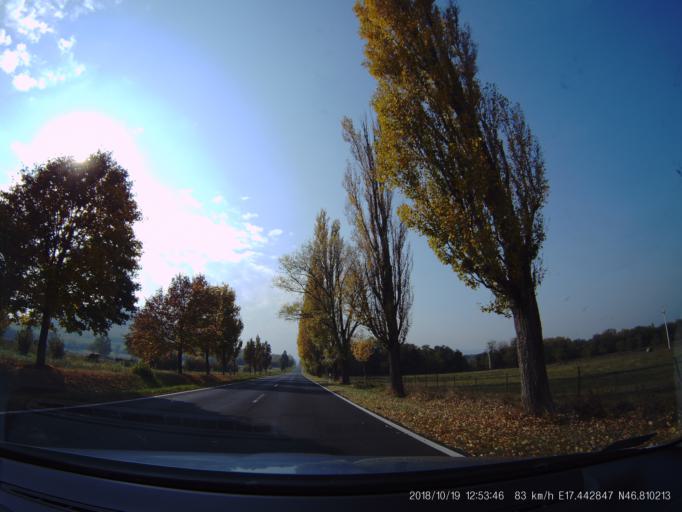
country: HU
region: Veszprem
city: Badacsonytomaj
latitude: 46.8102
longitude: 17.4427
